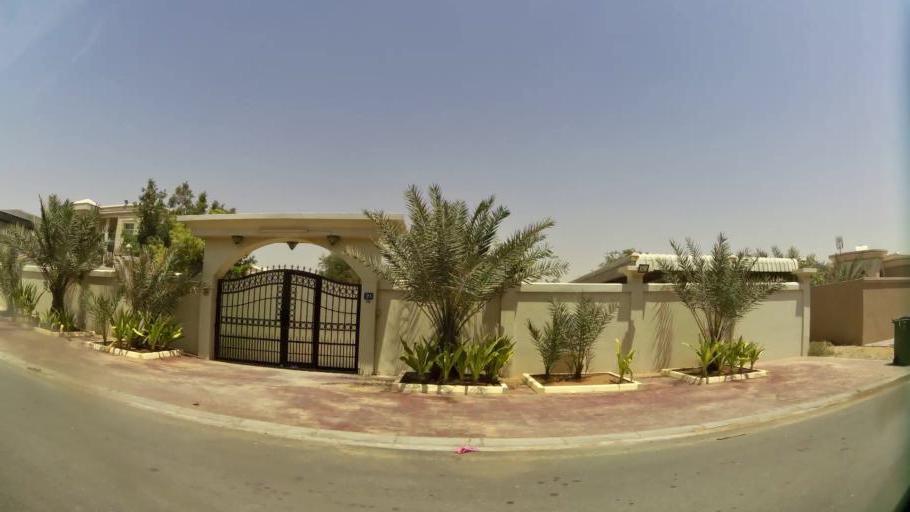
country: AE
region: Ajman
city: Ajman
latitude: 25.4207
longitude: 55.5054
